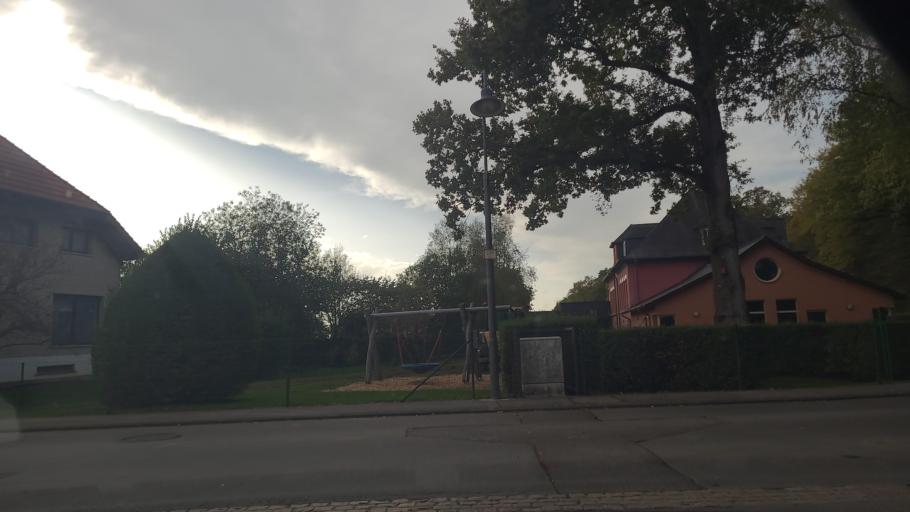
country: LU
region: Luxembourg
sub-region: Canton de Capellen
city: Kopstal
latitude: 49.6952
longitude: 6.0664
